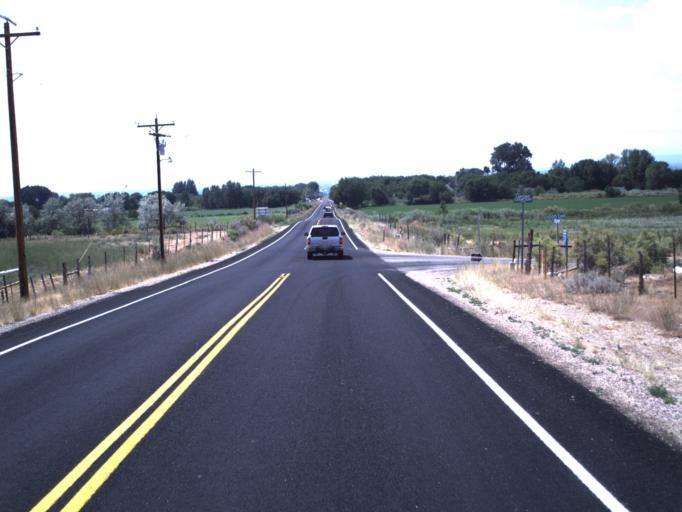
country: US
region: Utah
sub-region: Uintah County
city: Maeser
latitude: 40.4038
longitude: -109.7834
